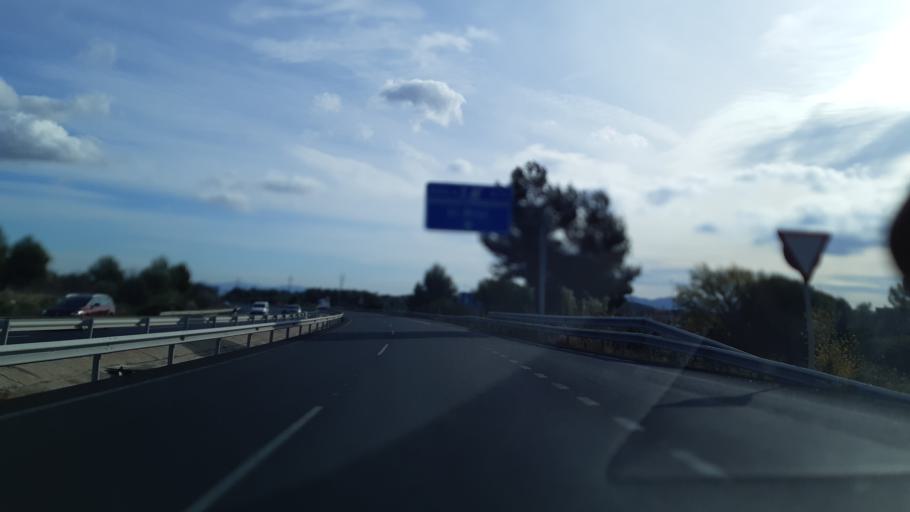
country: ES
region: Catalonia
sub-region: Provincia de Barcelona
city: Collbato
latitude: 41.5752
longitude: 1.7808
